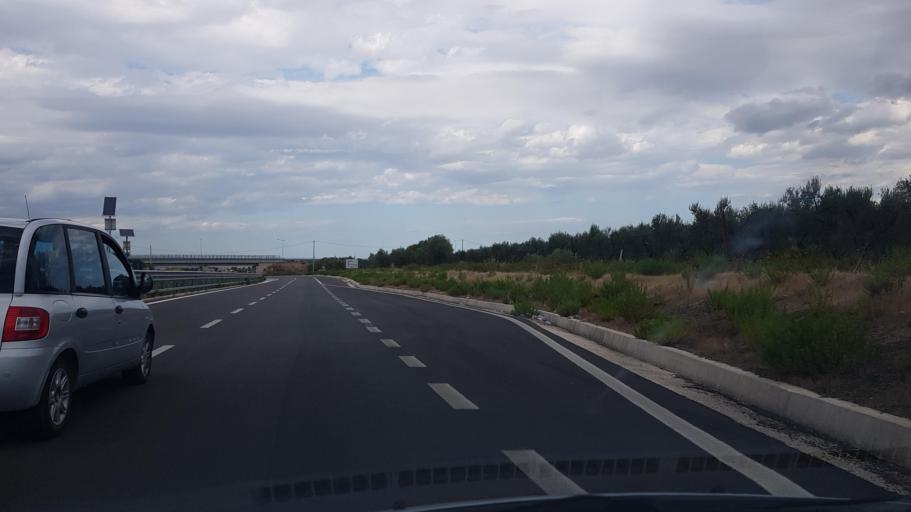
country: IT
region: Apulia
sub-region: Provincia di Taranto
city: Taranto
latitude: 40.4483
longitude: 17.2841
